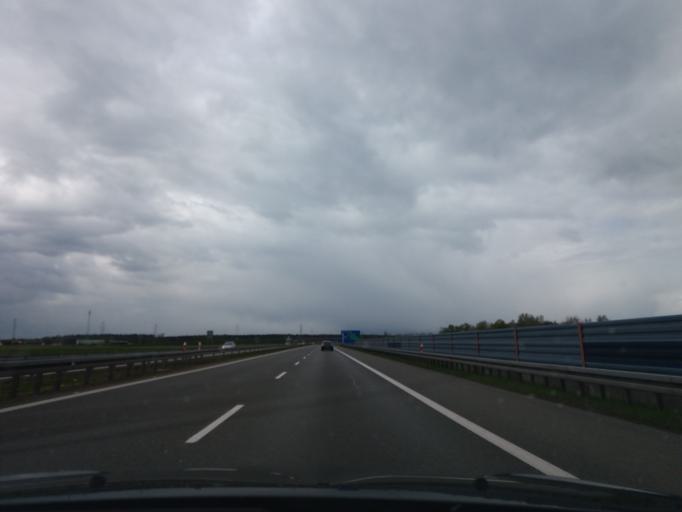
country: PL
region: Opole Voivodeship
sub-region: Powiat krapkowicki
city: Krapkowice
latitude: 50.5254
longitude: 17.9298
